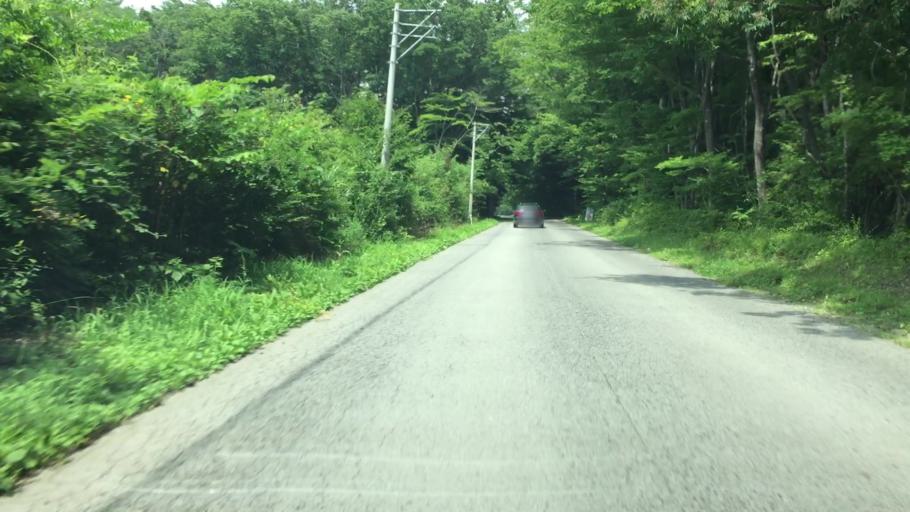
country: JP
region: Tochigi
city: Kuroiso
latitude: 37.0385
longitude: 139.9506
